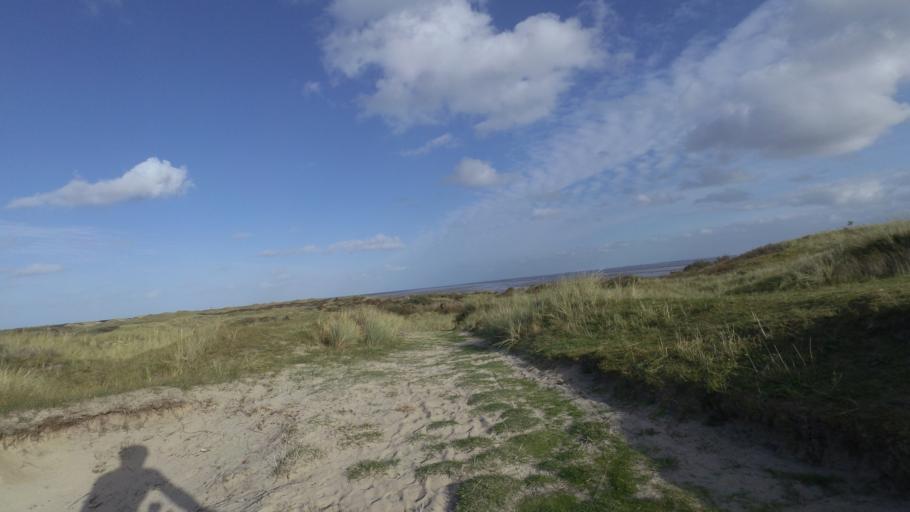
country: NL
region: Friesland
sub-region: Gemeente Dongeradeel
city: Holwerd
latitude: 53.4583
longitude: 5.9034
